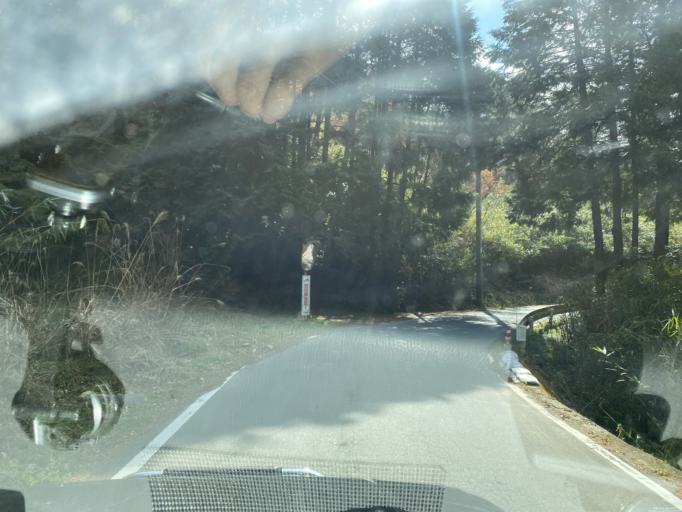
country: JP
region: Nara
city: Nara-shi
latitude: 34.7019
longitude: 135.9518
